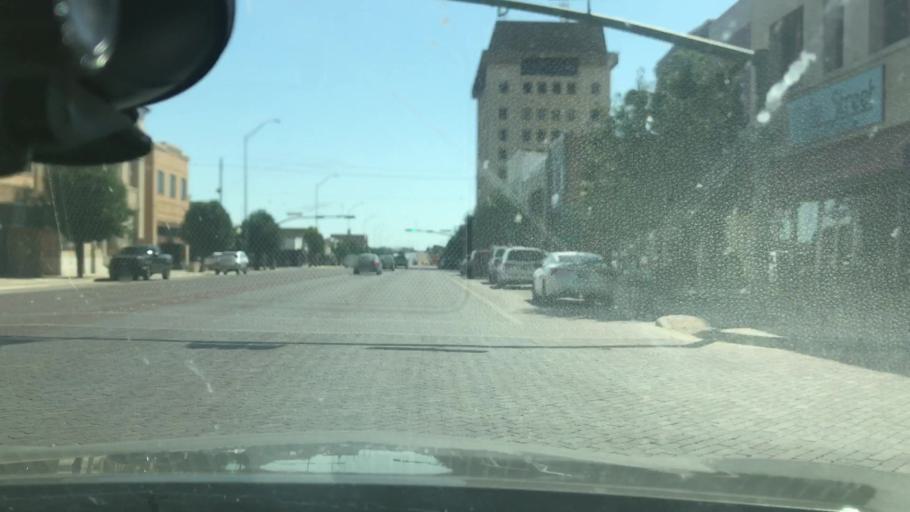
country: US
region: Texas
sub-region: Stephens County
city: Breckenridge
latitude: 32.7554
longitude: -98.9039
